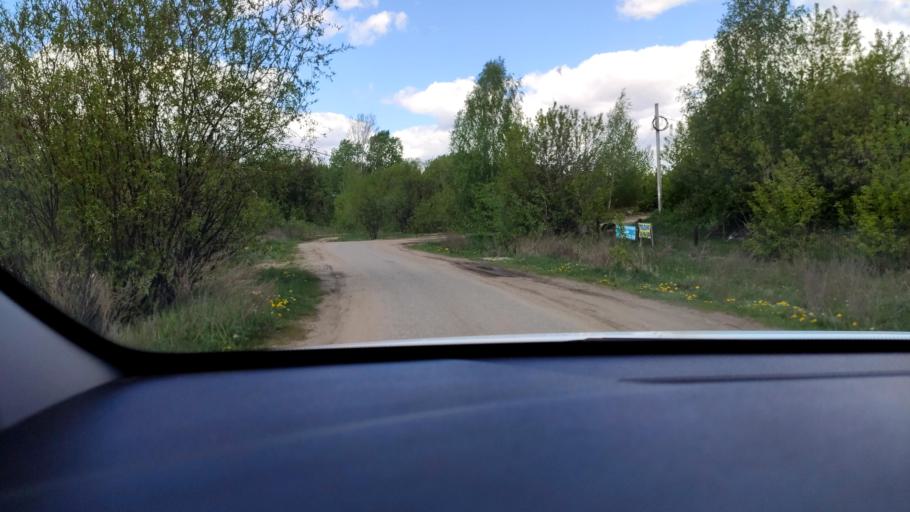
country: RU
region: Tatarstan
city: Stolbishchi
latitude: 55.7034
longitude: 49.1551
